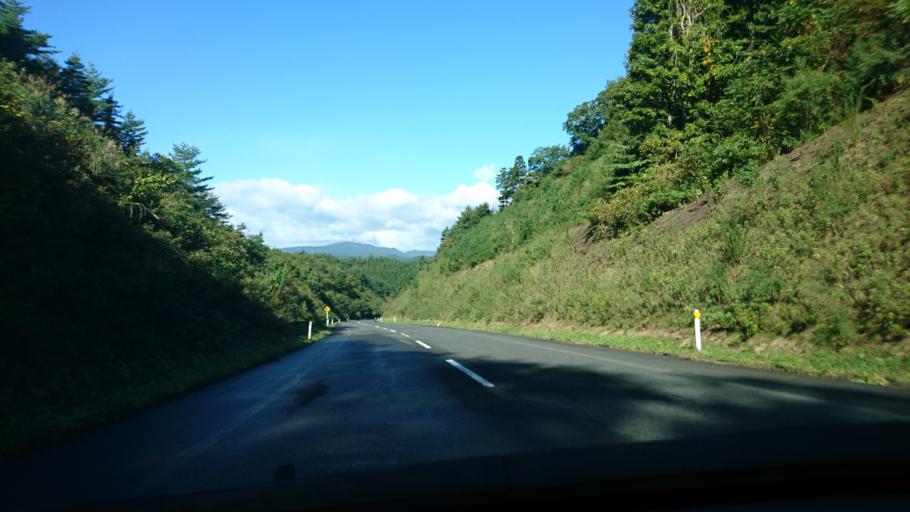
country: JP
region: Iwate
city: Ichinoseki
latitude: 39.0055
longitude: 141.0361
